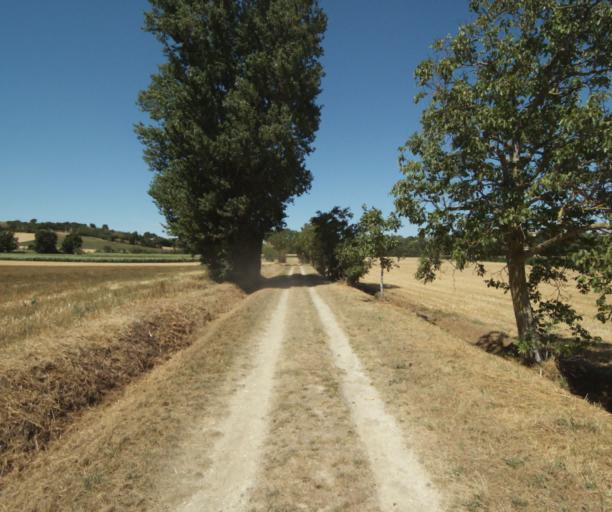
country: FR
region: Midi-Pyrenees
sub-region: Departement de la Haute-Garonne
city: Saint-Felix-Lauragais
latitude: 43.4729
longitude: 1.9231
